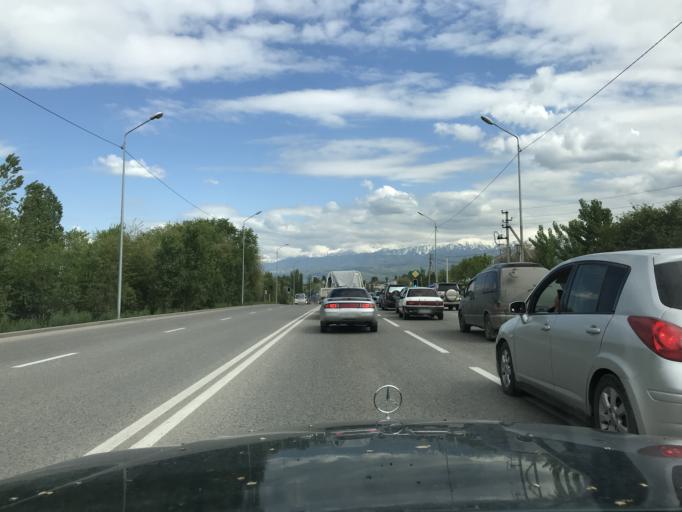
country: KZ
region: Almaty Oblysy
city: Burunday
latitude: 43.3114
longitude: 76.8654
